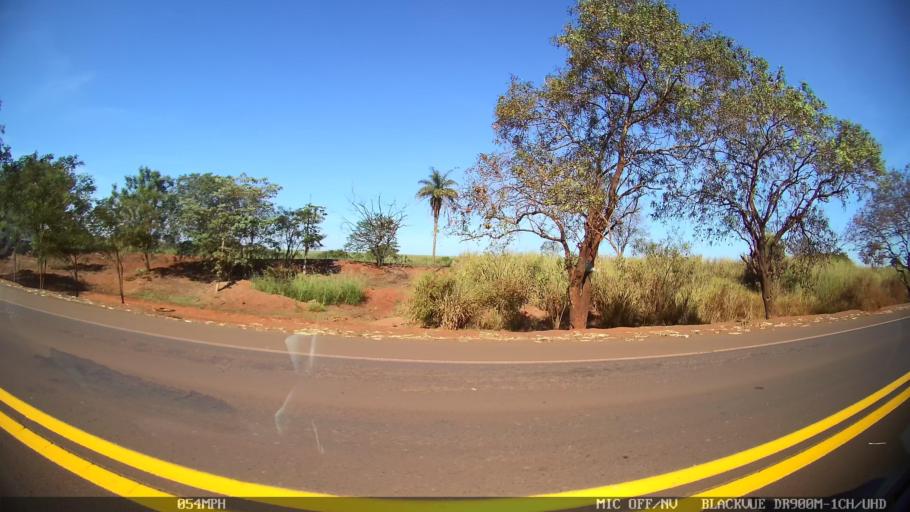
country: BR
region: Sao Paulo
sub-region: Barretos
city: Barretos
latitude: -20.4592
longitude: -48.4644
